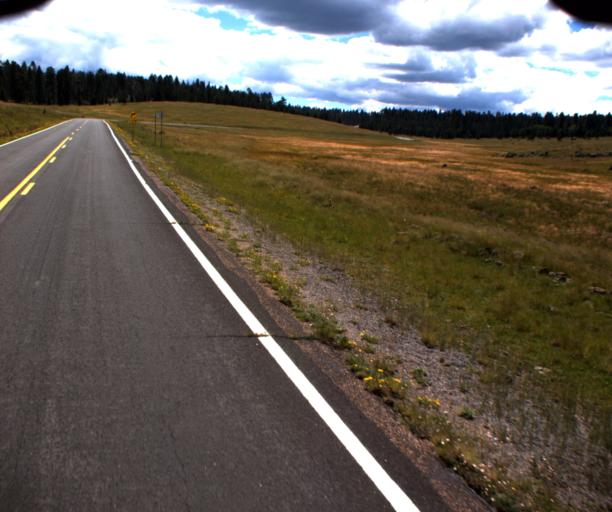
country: US
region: Arizona
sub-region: Apache County
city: Eagar
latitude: 33.8893
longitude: -109.4041
